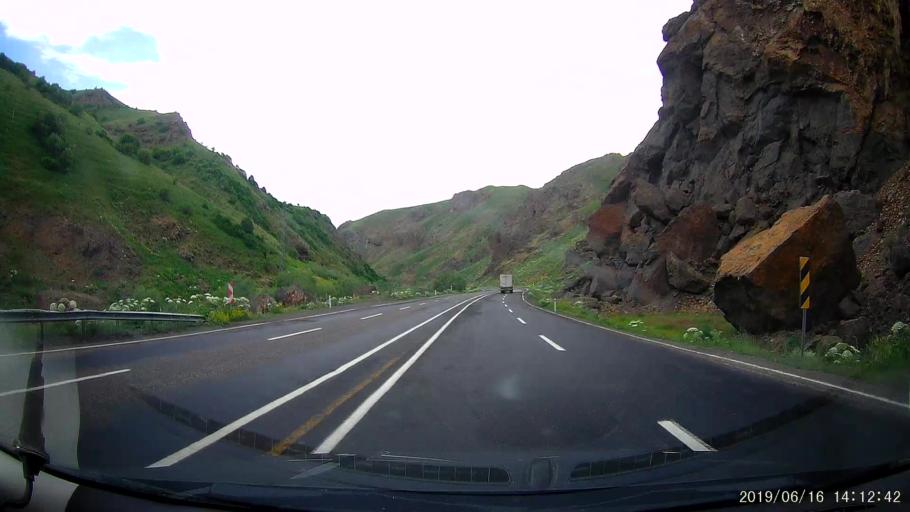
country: TR
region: Agri
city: Tahir
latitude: 39.7987
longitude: 42.5320
